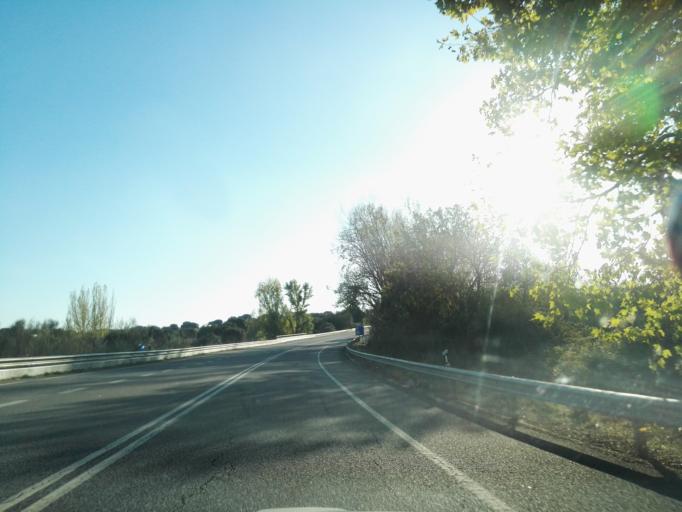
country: PT
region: Evora
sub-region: Vila Vicosa
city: Vila Vicosa
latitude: 38.8321
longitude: -7.4044
